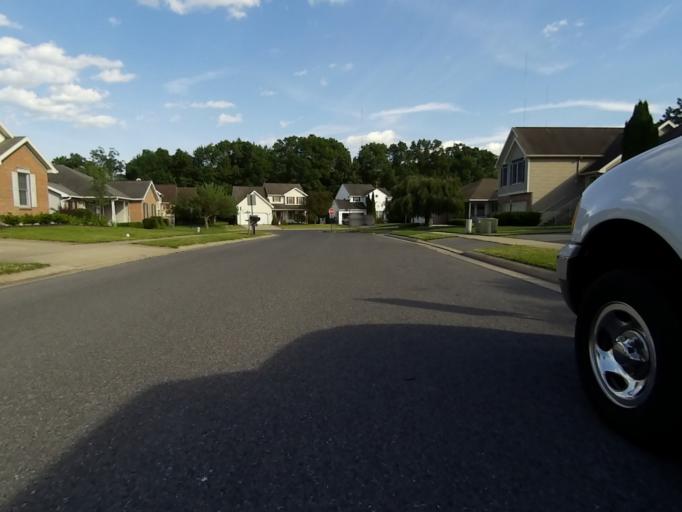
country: US
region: Pennsylvania
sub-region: Centre County
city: Park Forest Village
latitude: 40.8111
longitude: -77.9436
